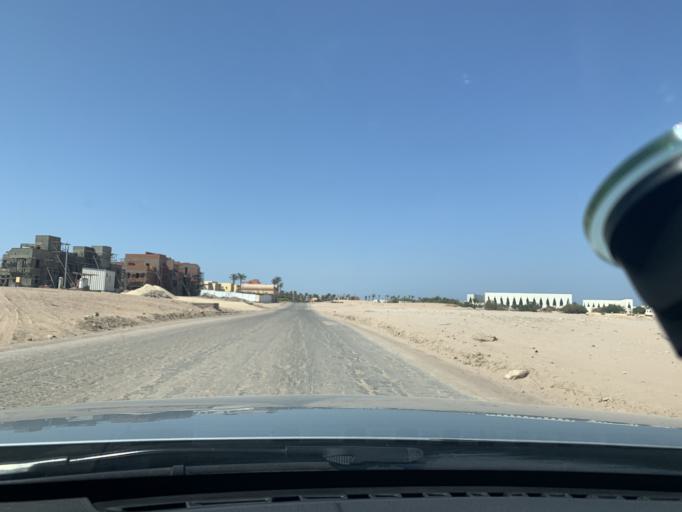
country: EG
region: Red Sea
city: El Gouna
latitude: 27.3999
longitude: 33.6630
